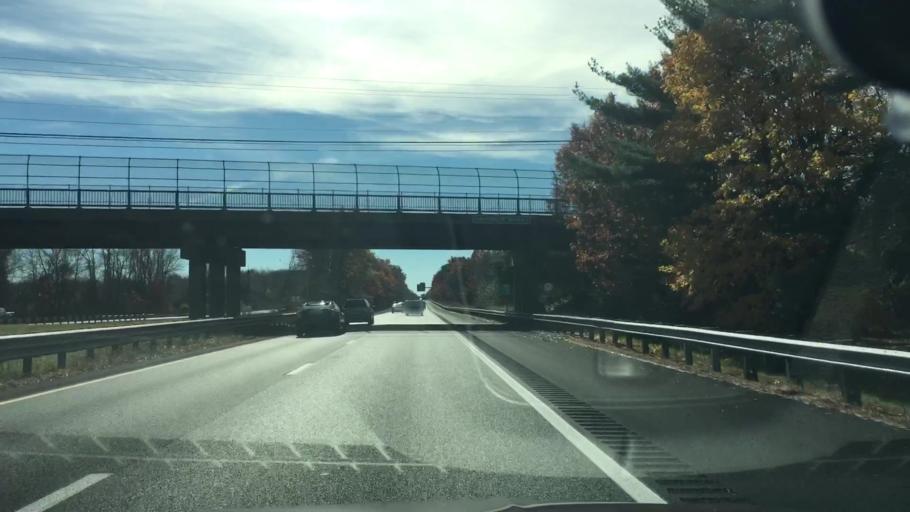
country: US
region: Massachusetts
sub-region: Franklin County
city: Whately
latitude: 42.4456
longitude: -72.6199
